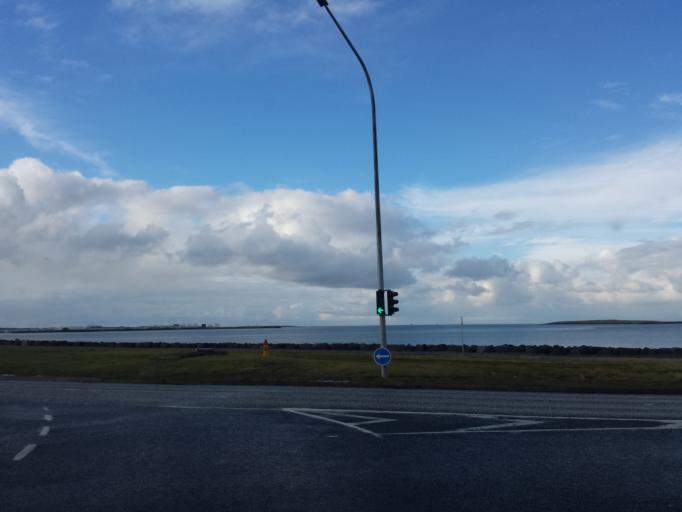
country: IS
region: Capital Region
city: Reykjavik
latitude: 64.1476
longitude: -21.8935
